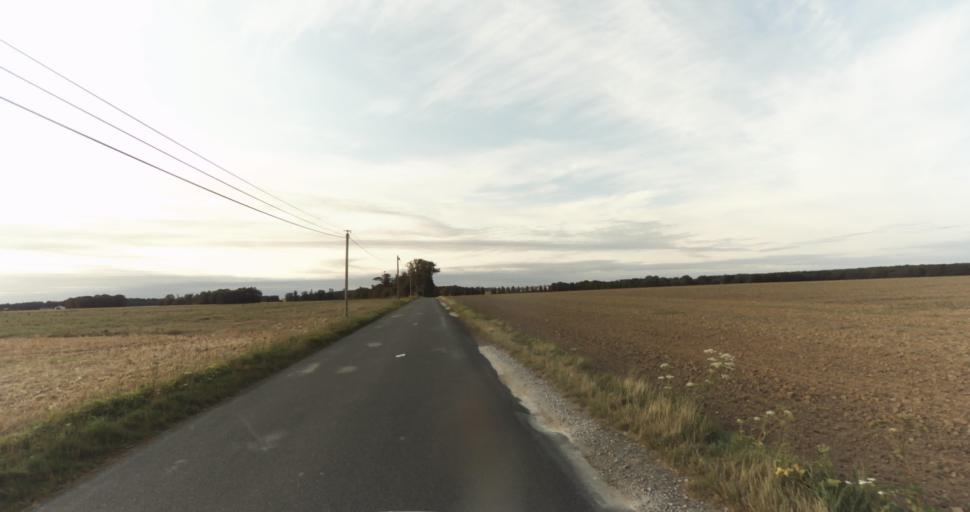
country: FR
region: Haute-Normandie
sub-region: Departement de l'Eure
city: Marcilly-sur-Eure
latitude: 48.8695
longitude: 1.2729
